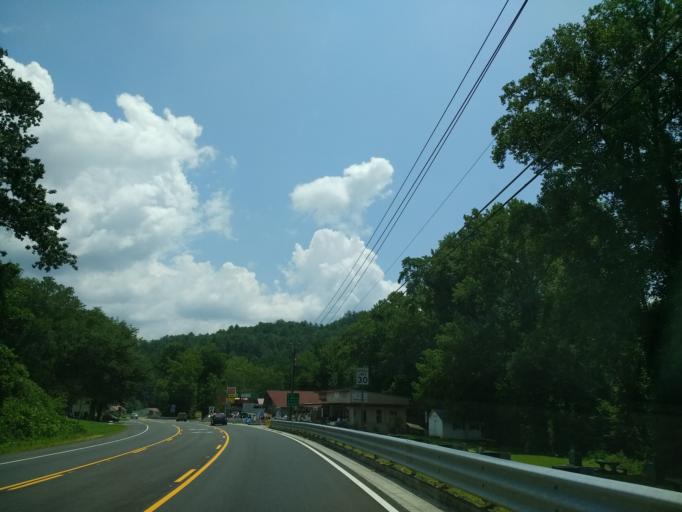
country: US
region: Georgia
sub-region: White County
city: Cleveland
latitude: 34.7104
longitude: -83.7424
